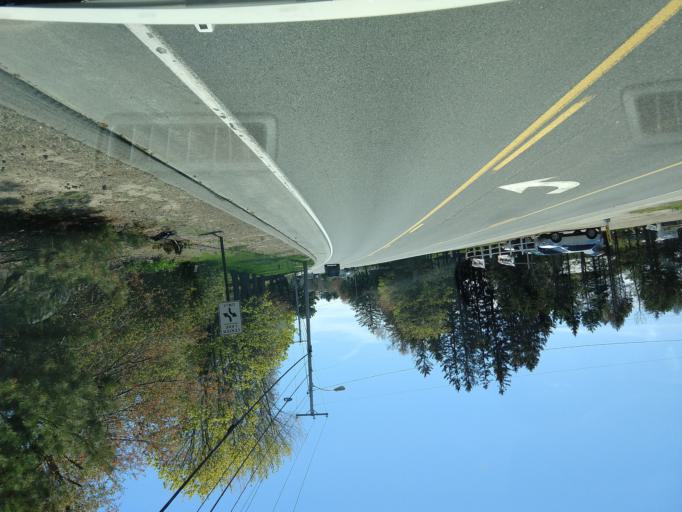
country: US
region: Maine
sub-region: York County
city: Wells Beach Station
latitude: 43.2905
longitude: -70.5910
